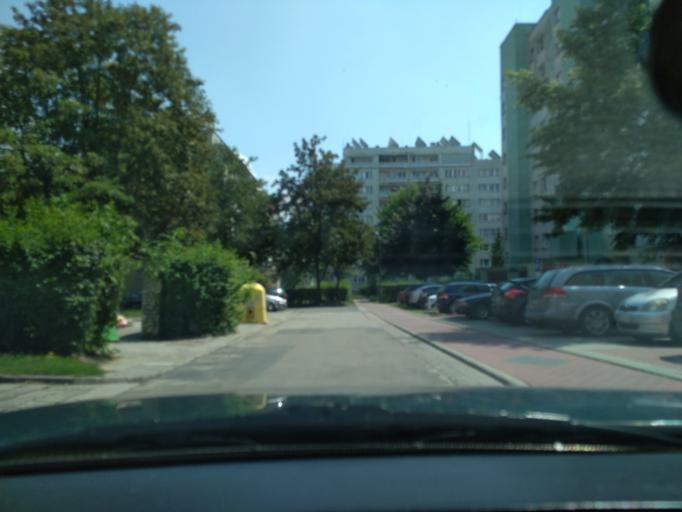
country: PL
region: Silesian Voivodeship
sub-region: Powiat raciborski
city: Raciborz
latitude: 50.0859
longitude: 18.1972
